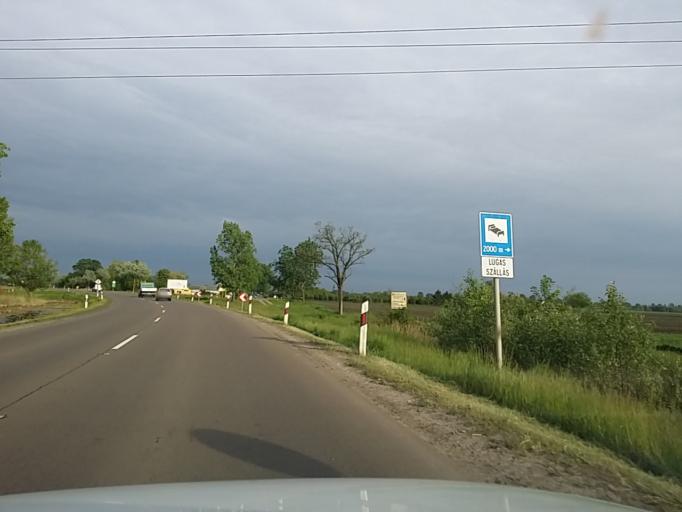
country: HU
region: Jasz-Nagykun-Szolnok
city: Jaszbereny
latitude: 47.5167
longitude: 19.8782
